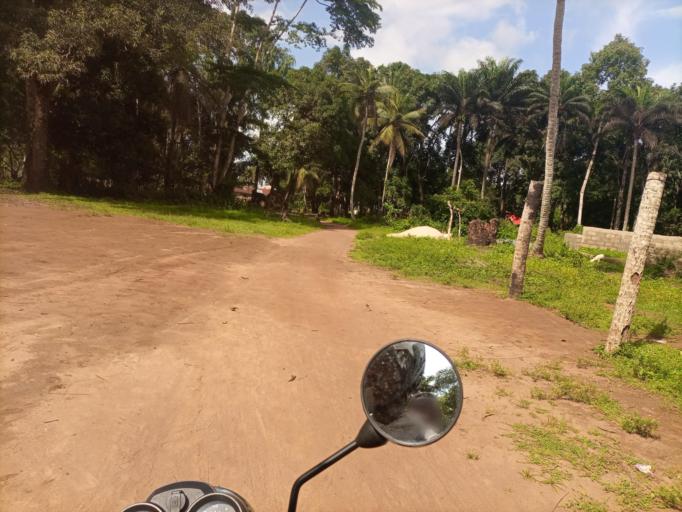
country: SL
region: Northern Province
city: Sawkta
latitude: 8.6294
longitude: -13.1845
